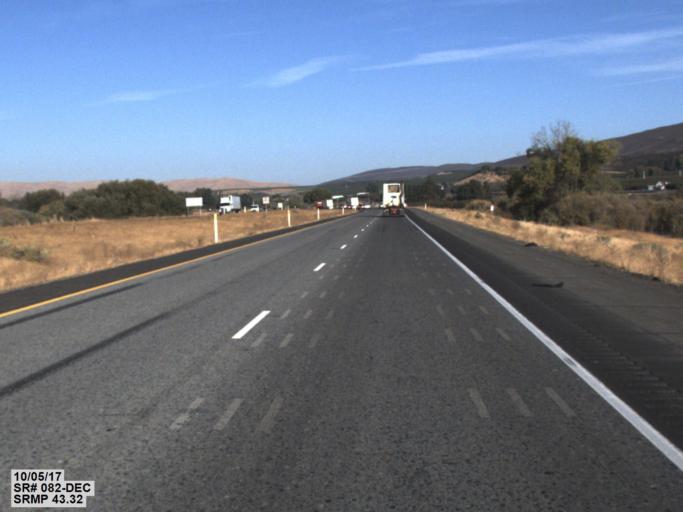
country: US
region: Washington
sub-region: Yakima County
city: Wapato
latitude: 46.4827
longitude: -120.4094
